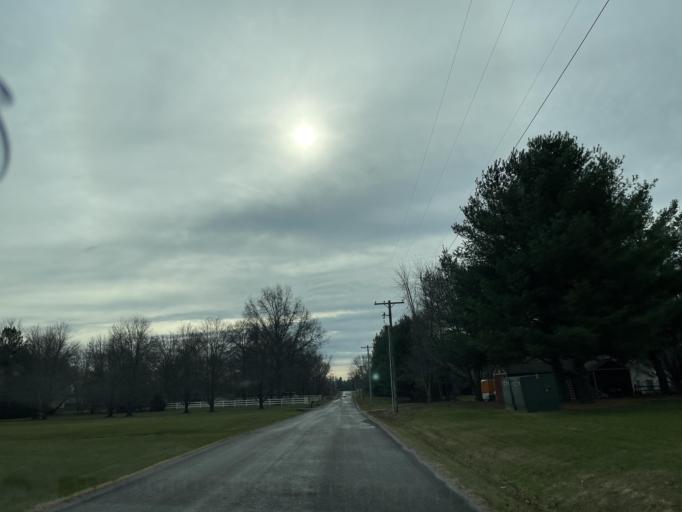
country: US
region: Illinois
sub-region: Sangamon County
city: Leland Grove
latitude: 39.7915
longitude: -89.7297
